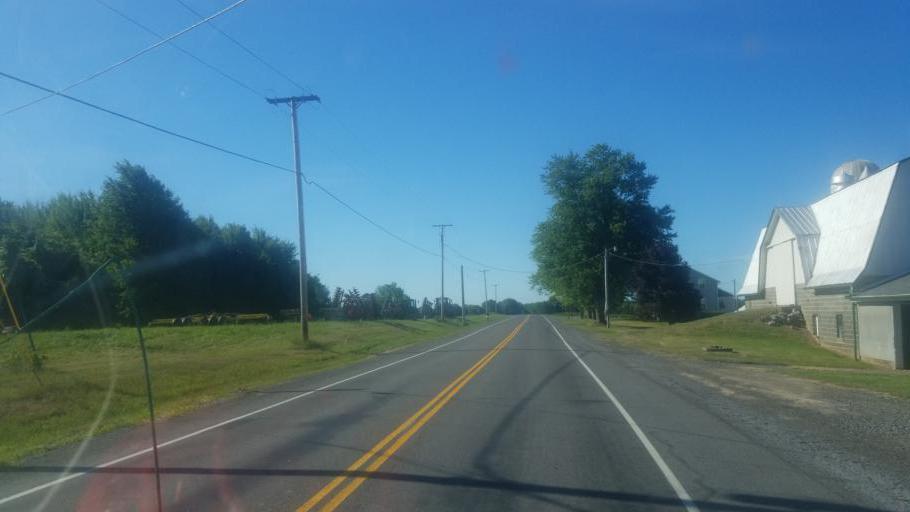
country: US
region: New York
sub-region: Ontario County
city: Phelps
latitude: 42.9164
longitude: -77.0627
